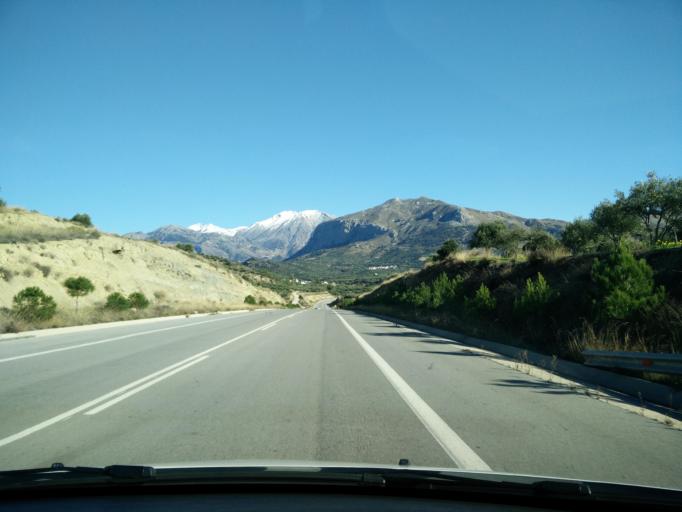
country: GR
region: Crete
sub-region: Nomos Irakleiou
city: Arkalochori
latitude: 35.0802
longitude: 25.3226
